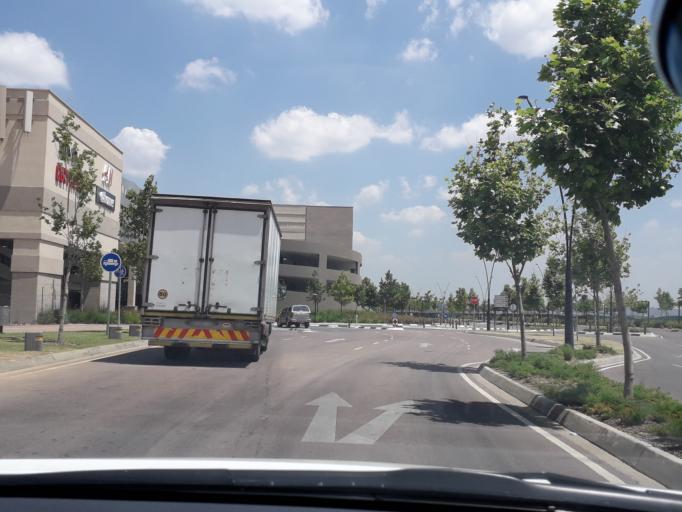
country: ZA
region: Gauteng
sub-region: City of Johannesburg Metropolitan Municipality
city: Midrand
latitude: -26.0126
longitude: 28.1062
